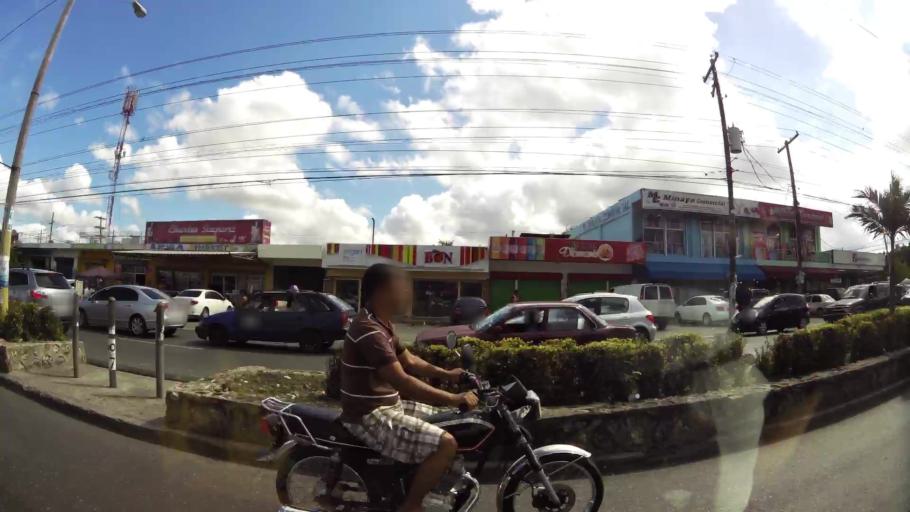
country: DO
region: Santo Domingo
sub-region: Santo Domingo
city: Santo Domingo Este
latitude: 18.5038
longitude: -69.8263
